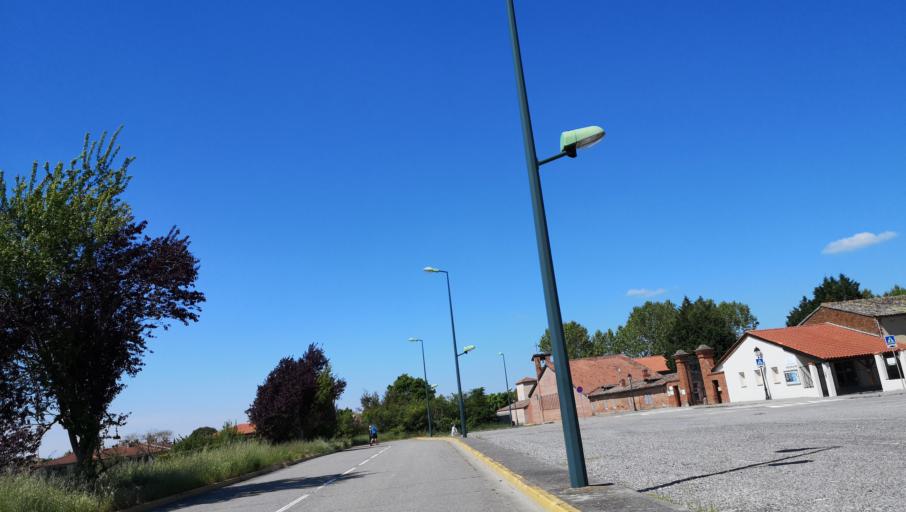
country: FR
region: Midi-Pyrenees
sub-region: Departement de la Haute-Garonne
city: Beauzelle
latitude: 43.6790
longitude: 1.3671
